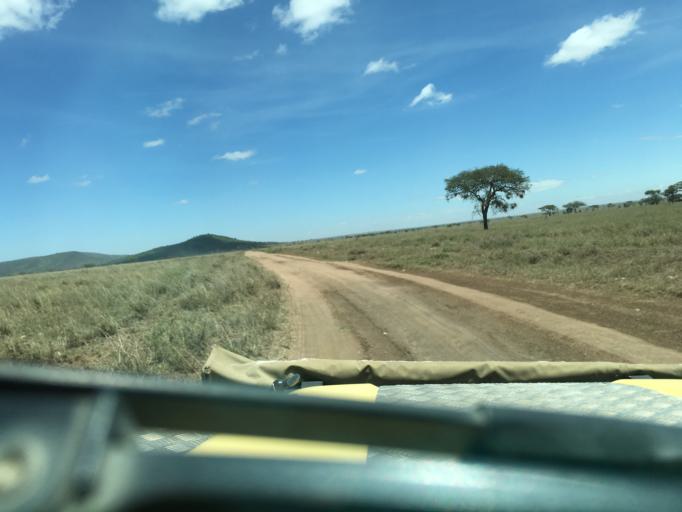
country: TZ
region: Simiyu
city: Kisesa
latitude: -2.6847
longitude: 34.7818
